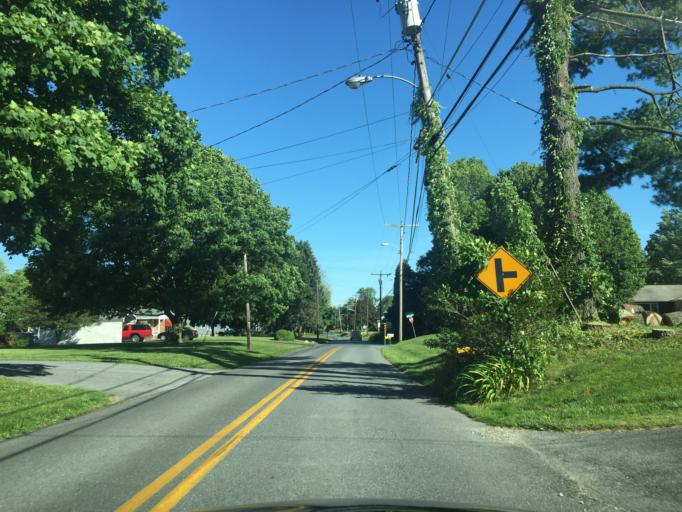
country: US
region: Maryland
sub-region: Carroll County
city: Hampstead
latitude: 39.5447
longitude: -76.8357
